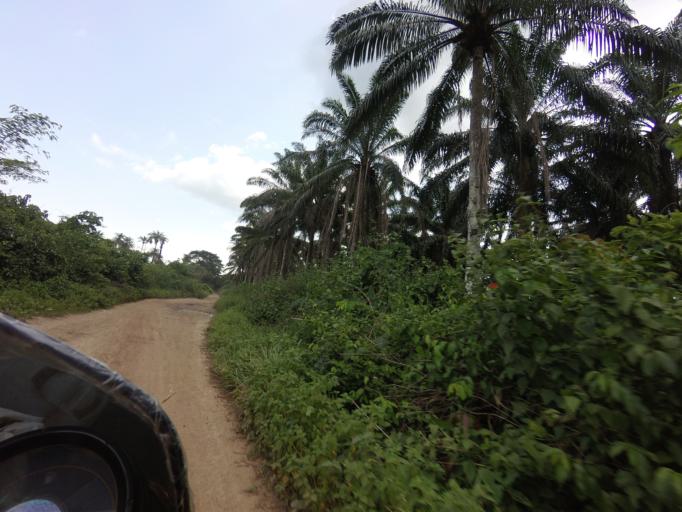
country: SL
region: Eastern Province
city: Manowa
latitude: 8.1544
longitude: -10.7554
